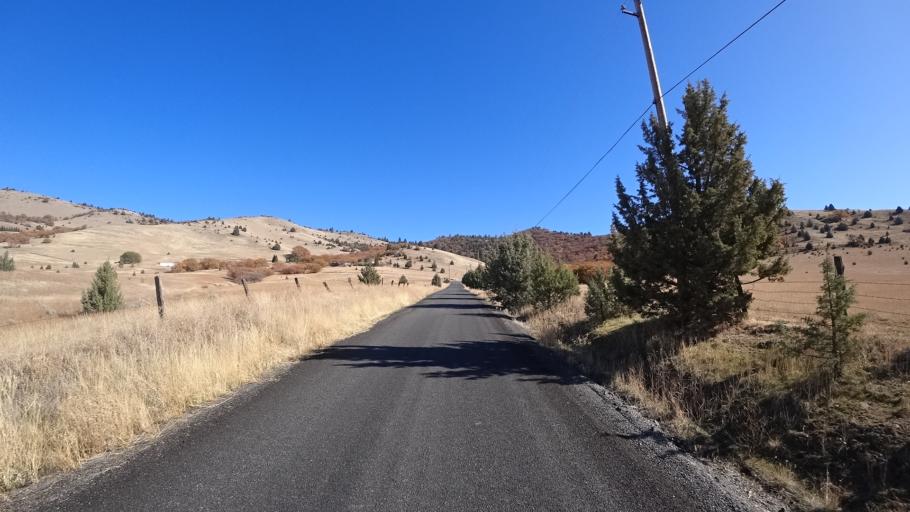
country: US
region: California
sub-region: Siskiyou County
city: Montague
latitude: 41.8305
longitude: -122.3458
